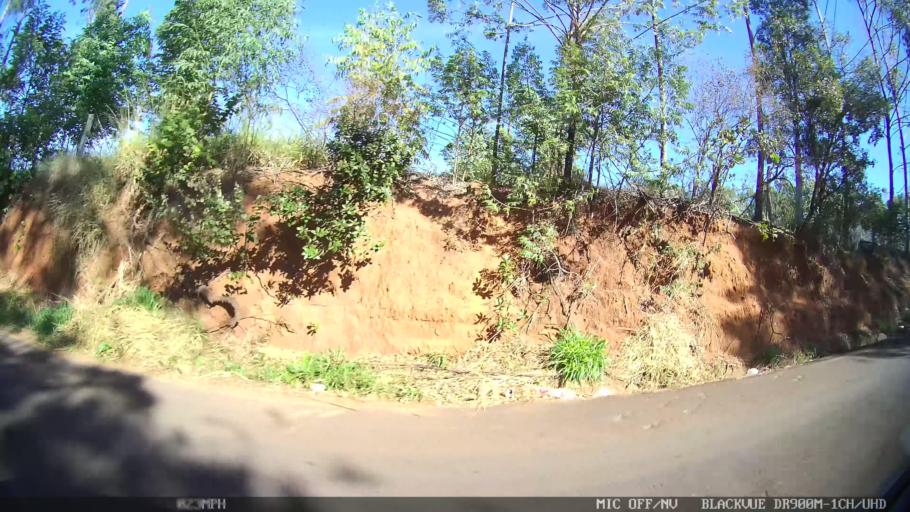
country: BR
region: Sao Paulo
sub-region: Franca
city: Franca
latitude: -20.5764
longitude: -47.3462
